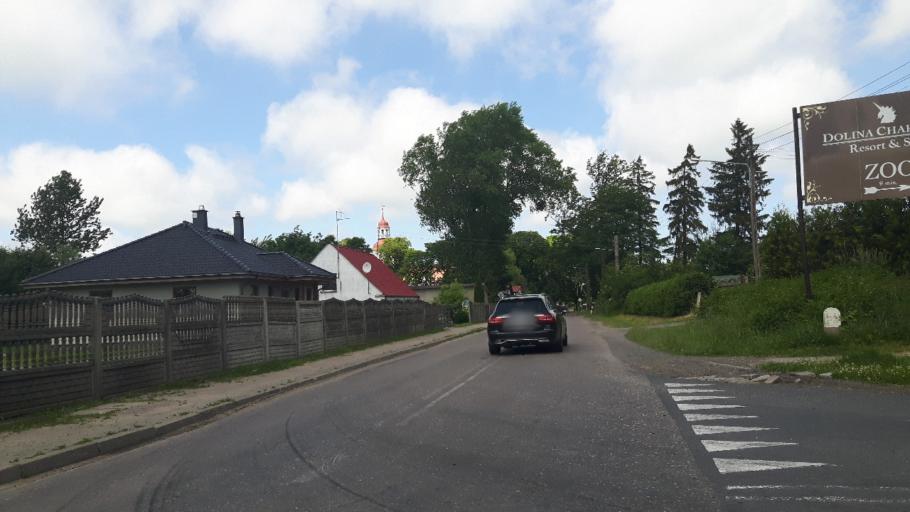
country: PL
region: Pomeranian Voivodeship
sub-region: Powiat slupski
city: Ustka
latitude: 54.5370
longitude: 16.8215
